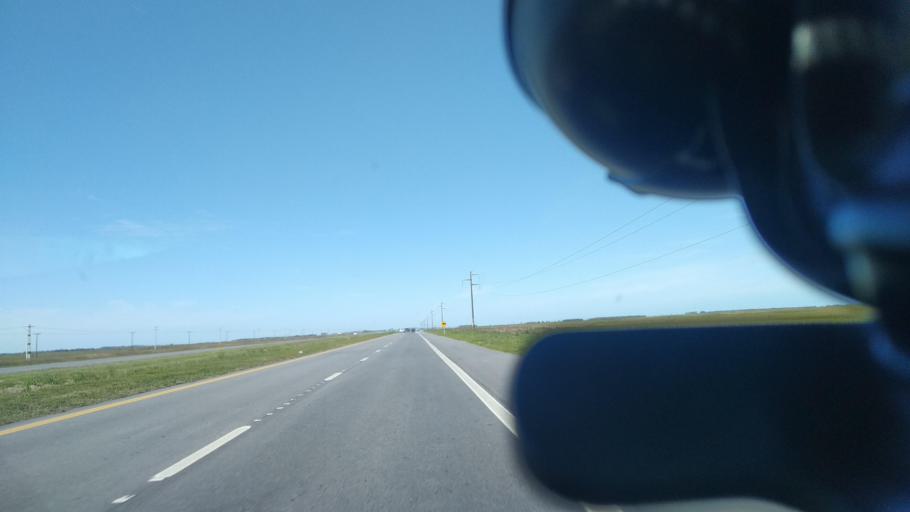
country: AR
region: Buenos Aires
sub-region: Partido de General Lavalle
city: General Lavalle
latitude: -36.4196
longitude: -56.8515
